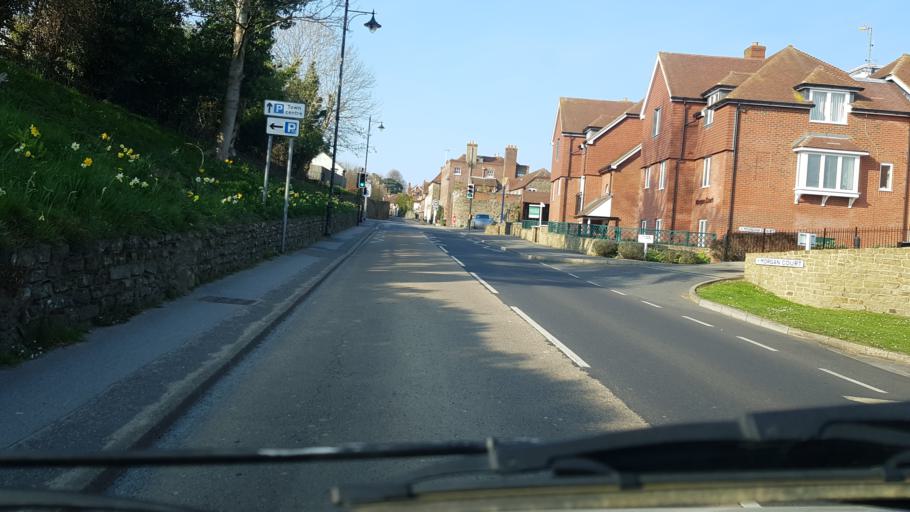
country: GB
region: England
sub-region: West Sussex
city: Petworth
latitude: 50.9833
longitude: -0.6114
